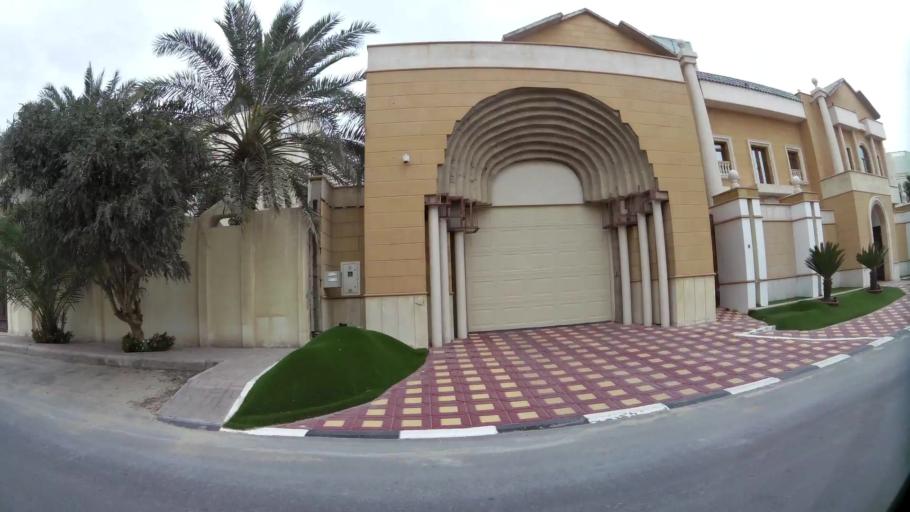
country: QA
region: Baladiyat ar Rayyan
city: Ar Rayyan
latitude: 25.3407
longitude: 51.4626
